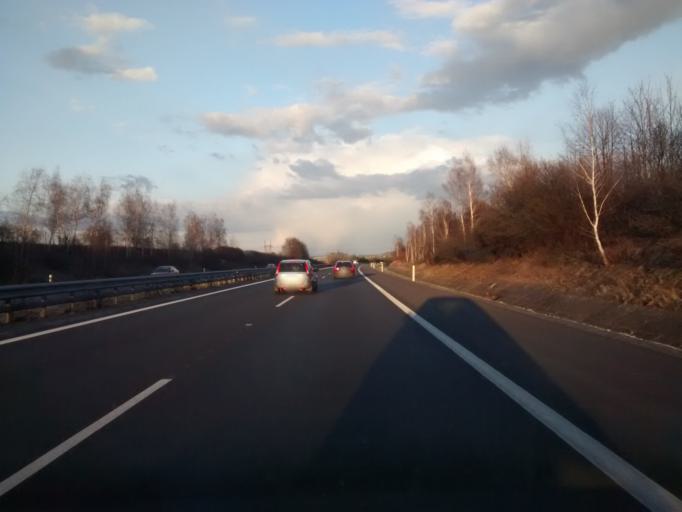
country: CZ
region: Central Bohemia
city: Celakovice
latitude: 50.1332
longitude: 14.7731
